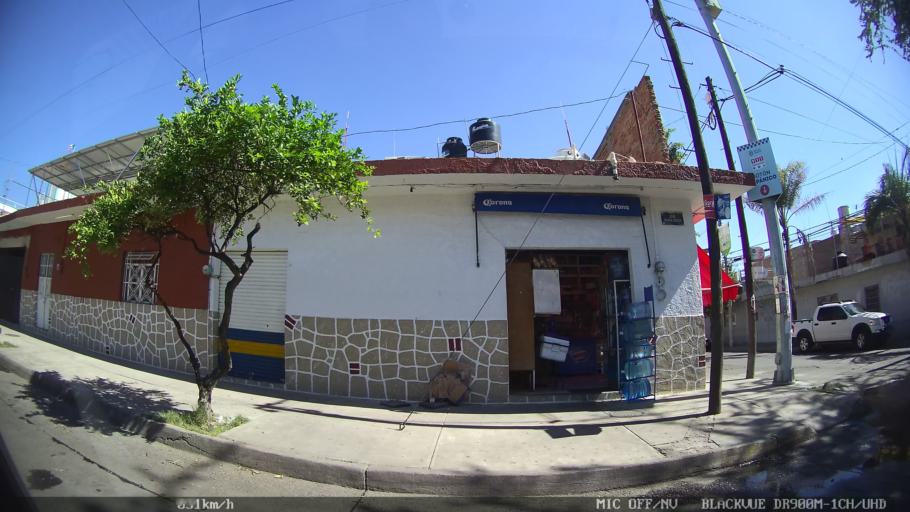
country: MX
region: Jalisco
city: Tlaquepaque
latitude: 20.6568
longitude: -103.2899
